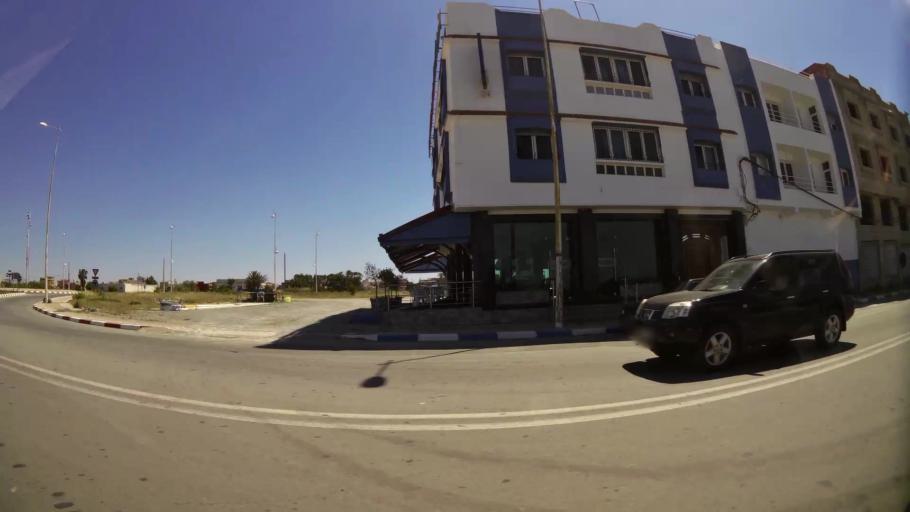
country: MA
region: Oriental
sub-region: Berkane-Taourirt
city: Madagh
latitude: 35.1362
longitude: -2.4131
